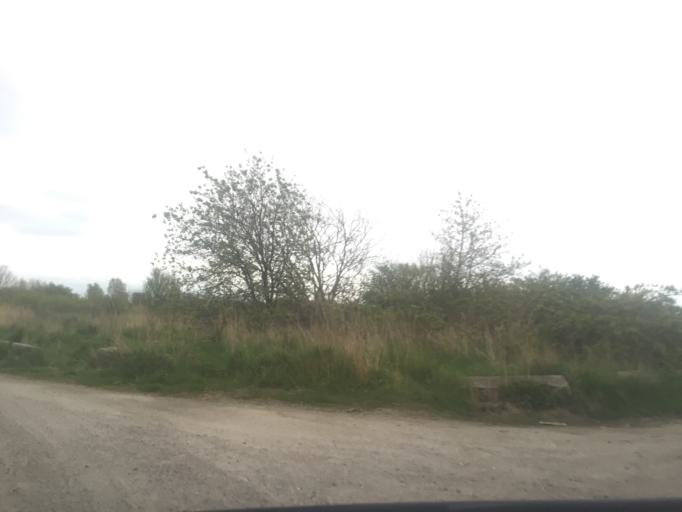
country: DK
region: Capital Region
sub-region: Frederiksberg Kommune
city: Frederiksberg
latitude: 55.6402
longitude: 12.5416
